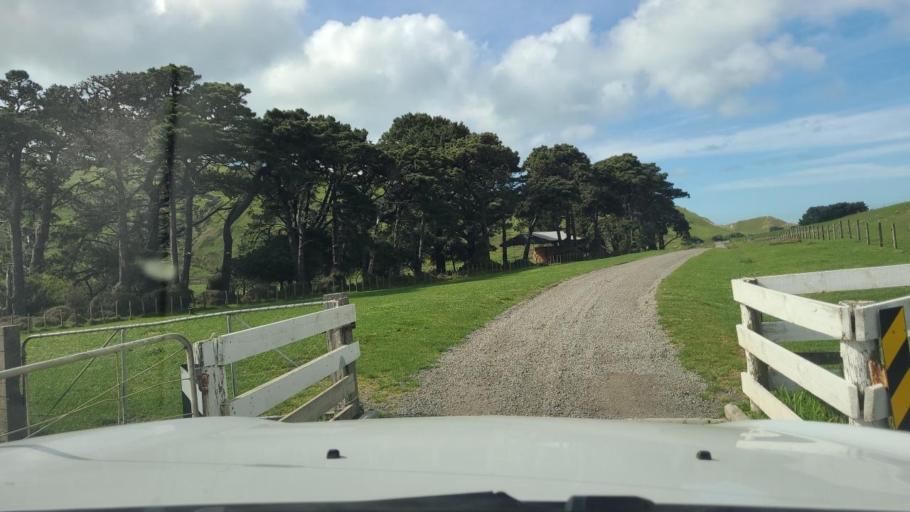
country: NZ
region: Wellington
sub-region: South Wairarapa District
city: Waipawa
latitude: -41.3796
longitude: 175.7246
